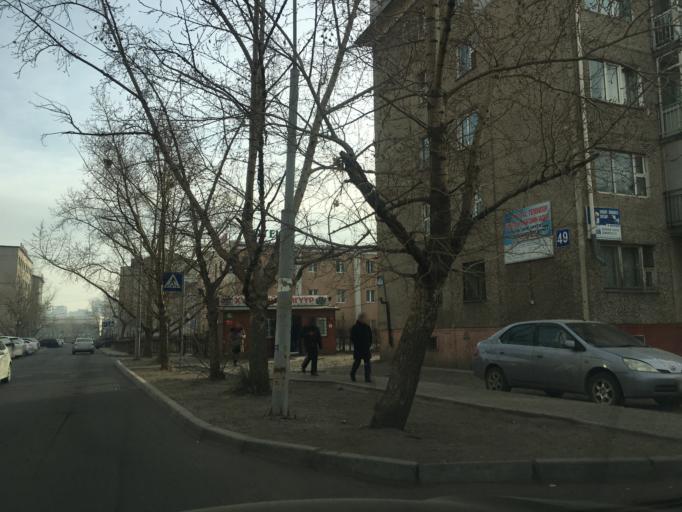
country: MN
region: Ulaanbaatar
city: Ulaanbaatar
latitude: 47.9125
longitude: 106.8879
